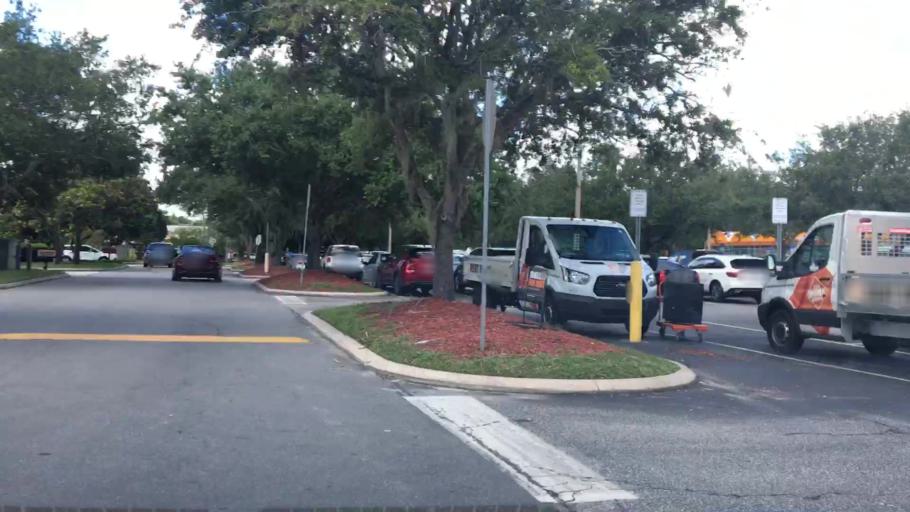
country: US
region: Florida
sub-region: Seminole County
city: Heathrow
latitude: 28.7571
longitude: -81.3563
